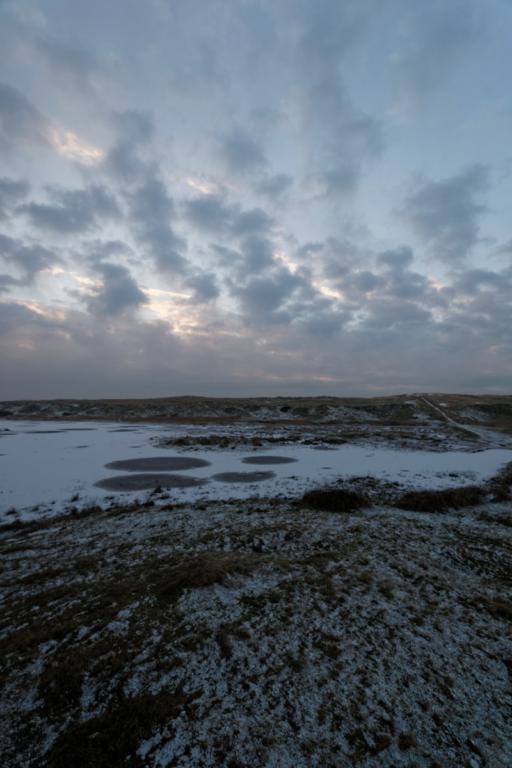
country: NL
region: North Holland
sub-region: Gemeente Texel
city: Den Burg
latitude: 53.0323
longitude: 4.7155
